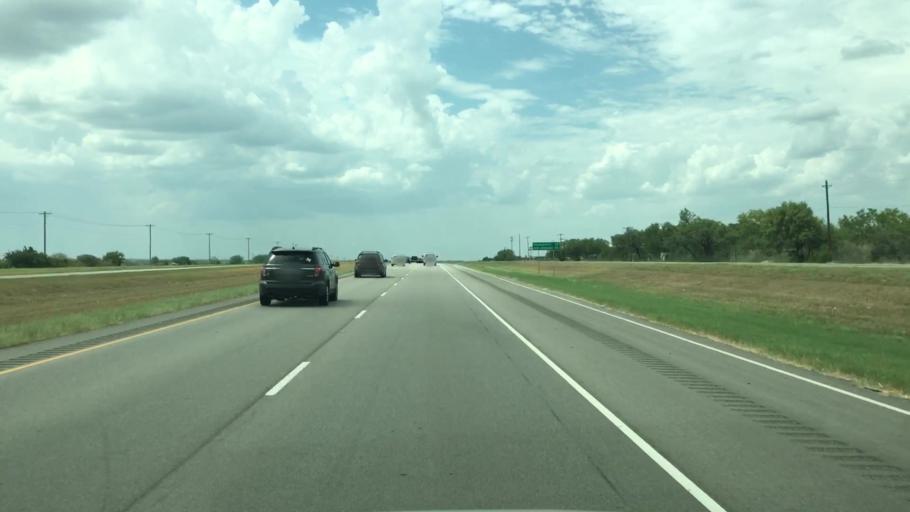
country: US
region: Texas
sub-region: Live Oak County
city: Three Rivers
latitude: 28.4995
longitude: -98.1544
